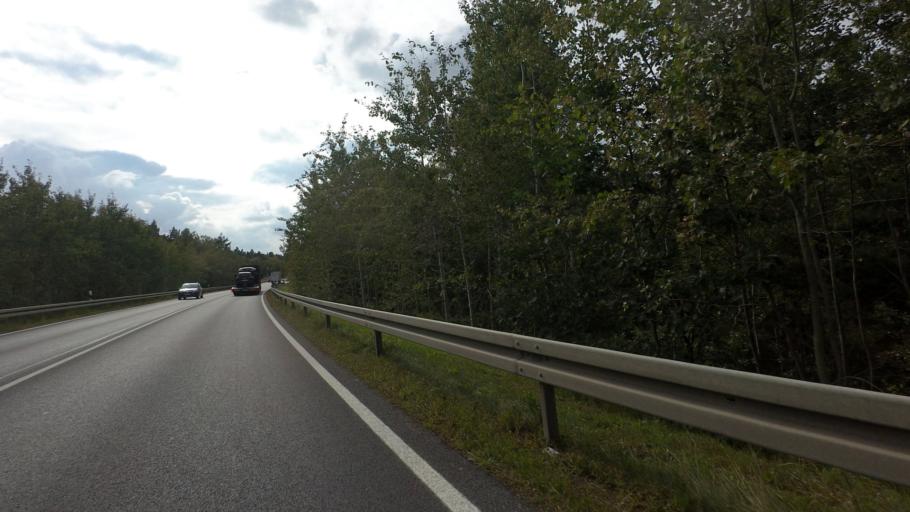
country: DE
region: Brandenburg
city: Grossraschen
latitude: 51.5731
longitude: 14.0780
